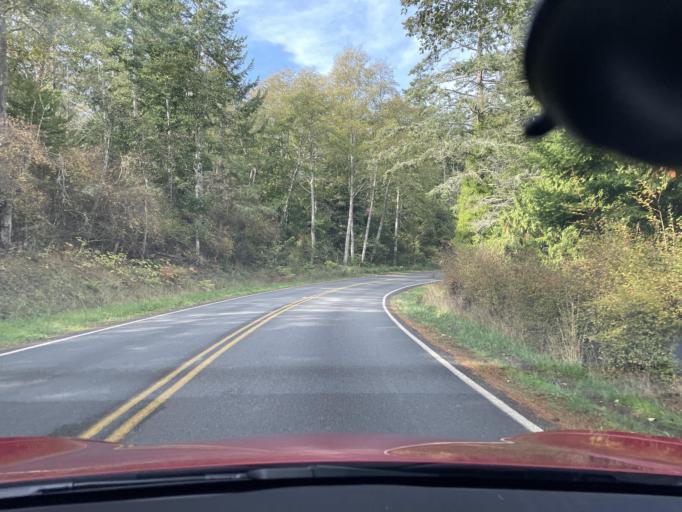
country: US
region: Washington
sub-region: San Juan County
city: Friday Harbor
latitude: 48.5277
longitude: -123.0041
